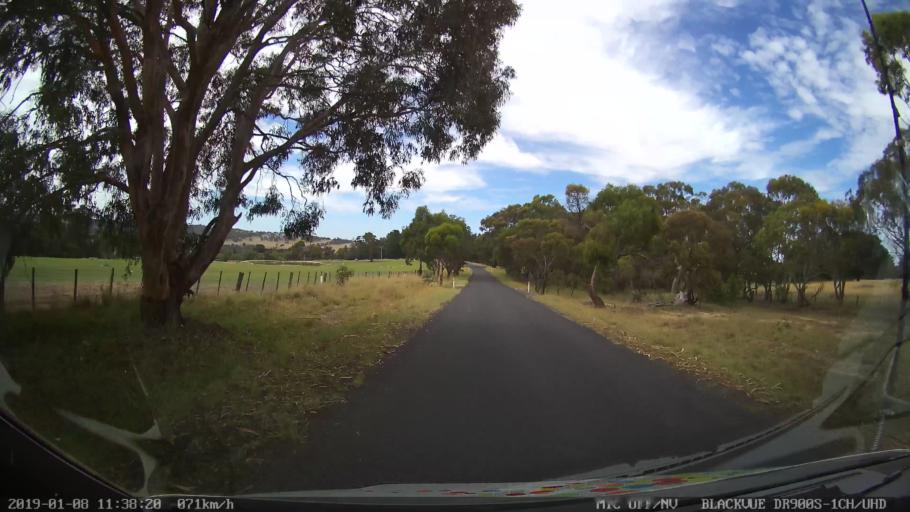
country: AU
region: New South Wales
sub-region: Guyra
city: Guyra
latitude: -30.3598
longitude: 151.5552
